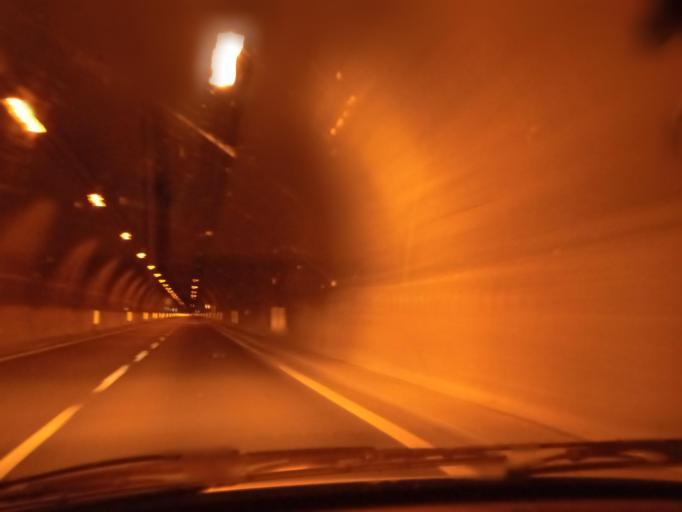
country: IT
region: Sicily
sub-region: Palermo
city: Finale
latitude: 38.0073
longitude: 14.1862
